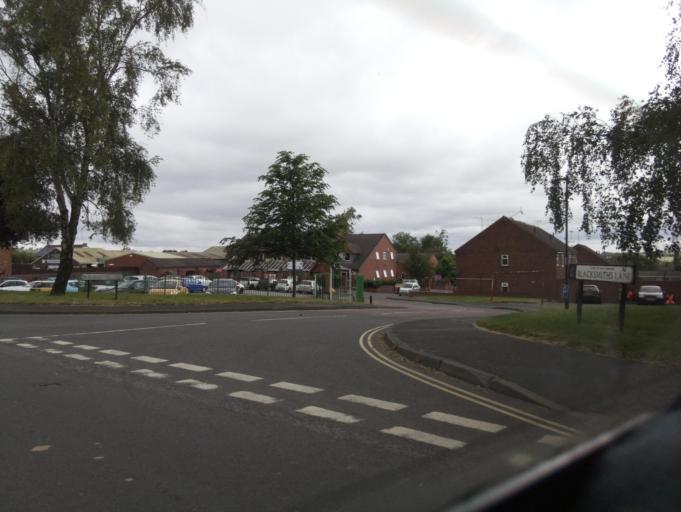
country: GB
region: England
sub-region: Derbyshire
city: Swadlincote
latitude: 52.7681
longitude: -1.5325
